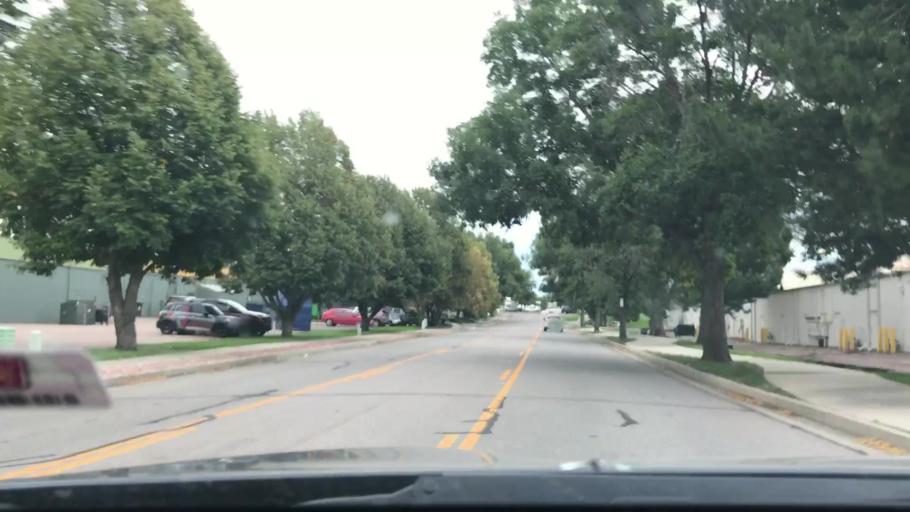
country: US
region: Colorado
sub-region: El Paso County
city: Cimarron Hills
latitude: 38.8897
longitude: -104.7595
